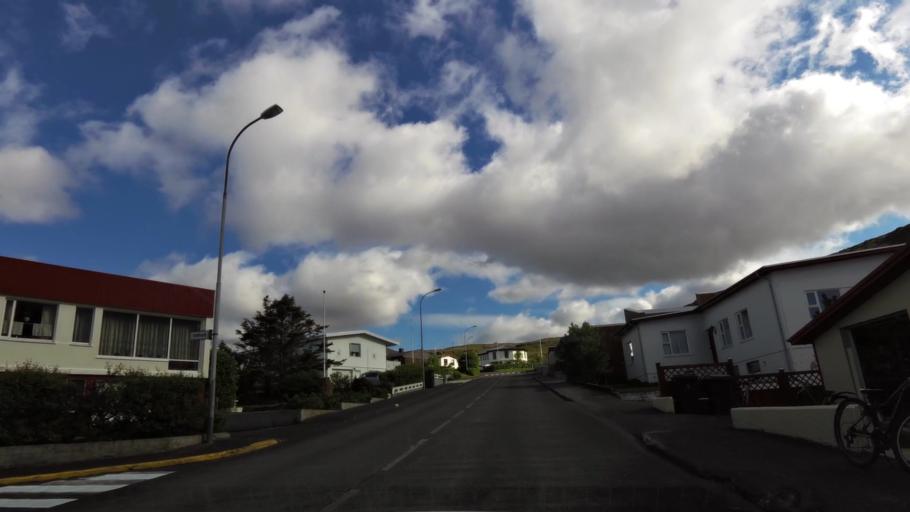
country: IS
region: West
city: Olafsvik
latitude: 64.8922
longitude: -23.7095
